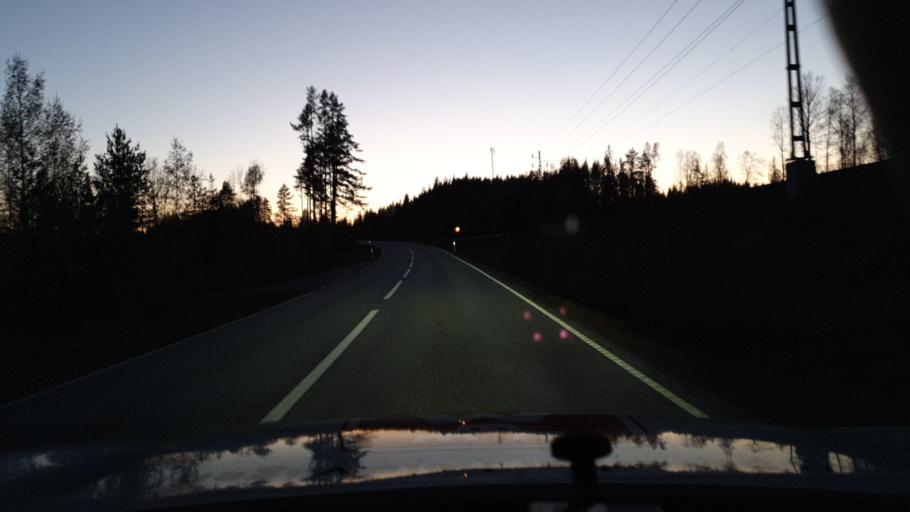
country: SE
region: OErebro
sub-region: Hallefors Kommun
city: Haellefors
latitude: 59.8187
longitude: 14.6479
